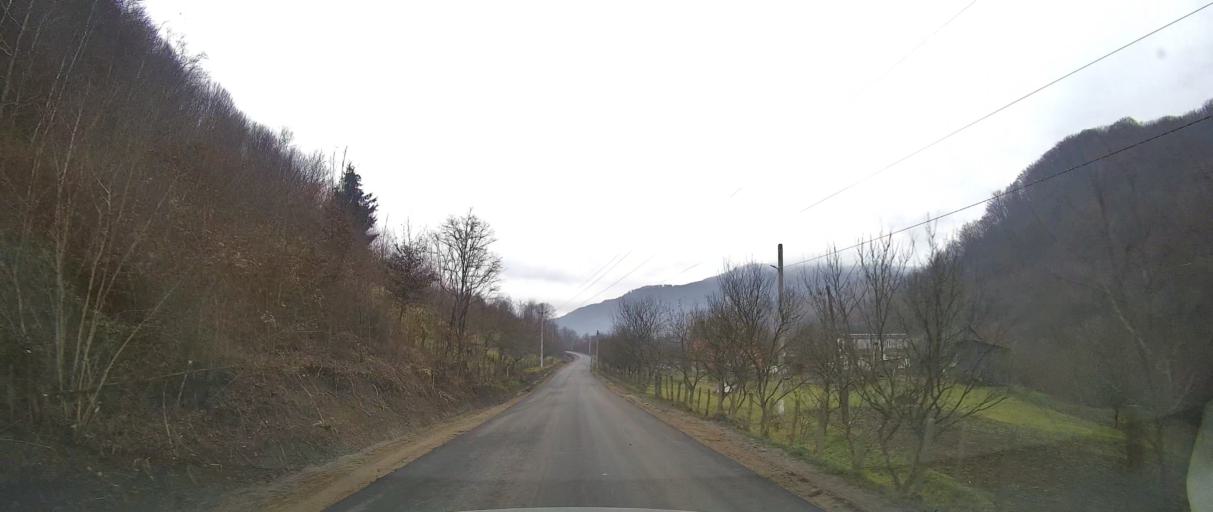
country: UA
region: Zakarpattia
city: Velykyi Bereznyi
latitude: 48.9585
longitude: 22.5475
